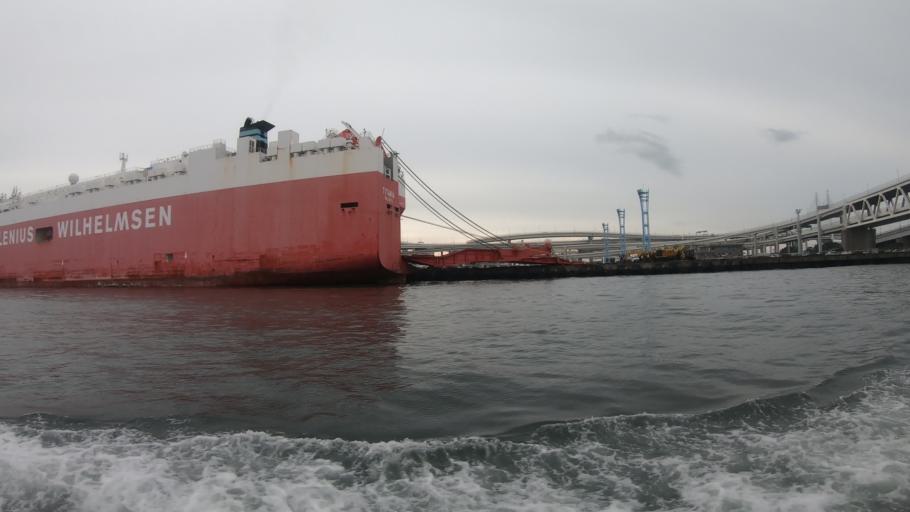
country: JP
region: Kanagawa
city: Yokohama
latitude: 35.4685
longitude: 139.6779
